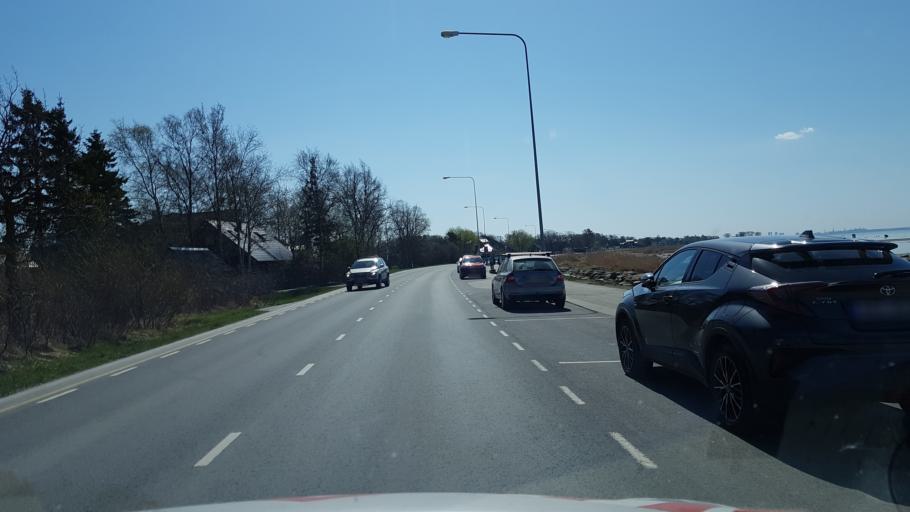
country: EE
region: Harju
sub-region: Viimsi vald
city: Rummu
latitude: 59.5536
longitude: 24.7943
